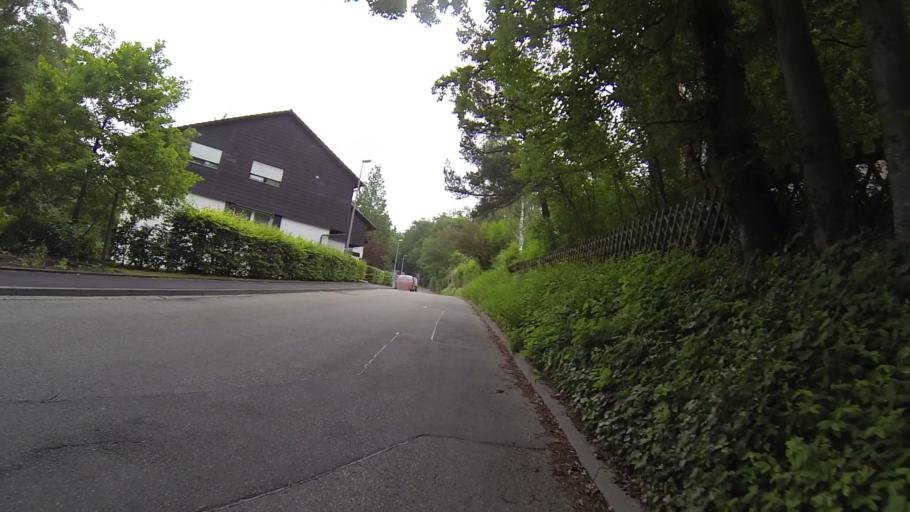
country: DE
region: Baden-Wuerttemberg
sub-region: Tuebingen Region
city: Dornstadt
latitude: 48.4195
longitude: 9.8908
